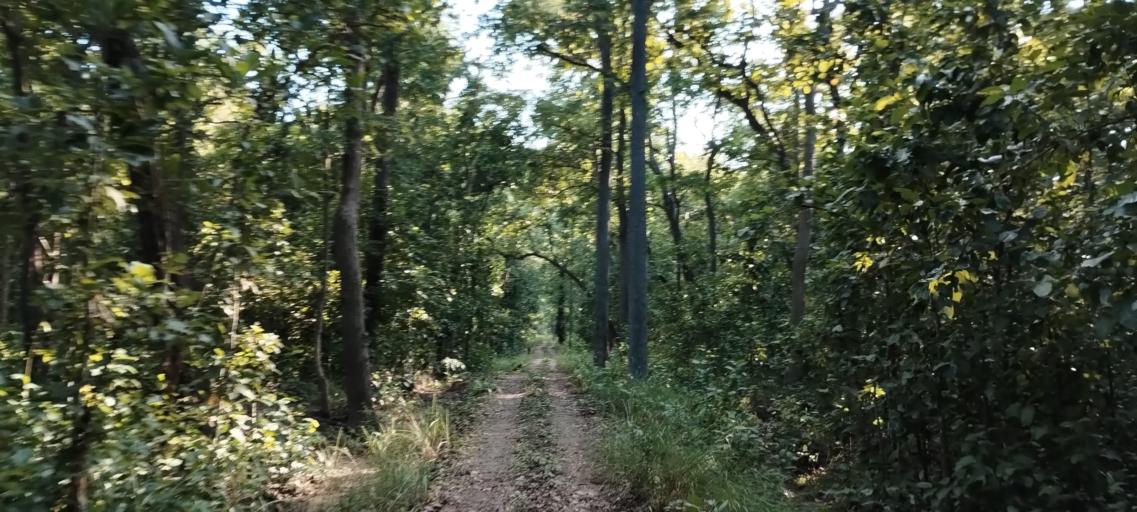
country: NP
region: Far Western
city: Tikapur
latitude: 28.5122
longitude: 81.2707
